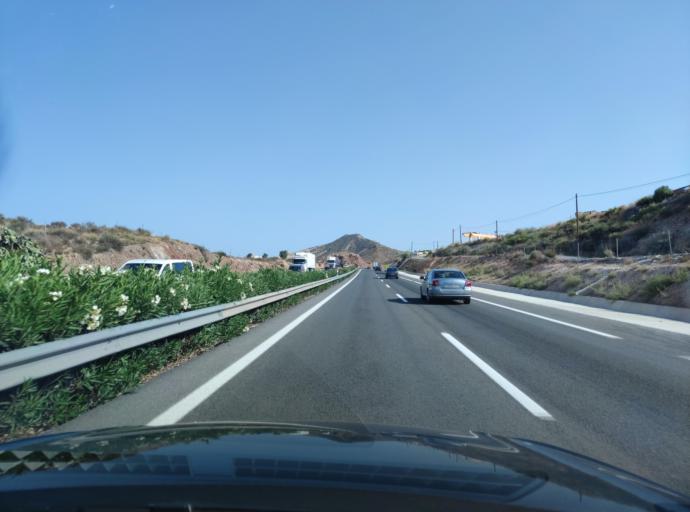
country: ES
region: Valencia
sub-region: Provincia de Alicante
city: Novelda
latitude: 38.4210
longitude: -0.7817
